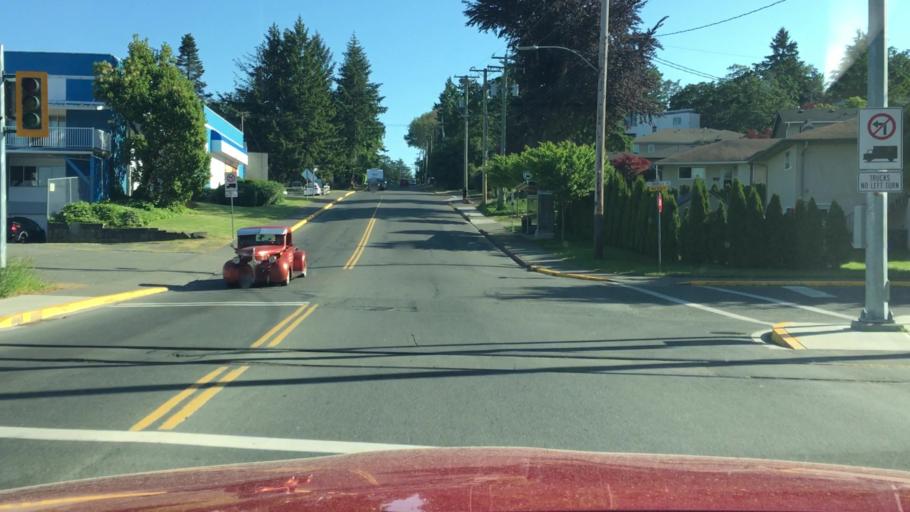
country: CA
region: British Columbia
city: Victoria
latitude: 48.4370
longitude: -123.4026
